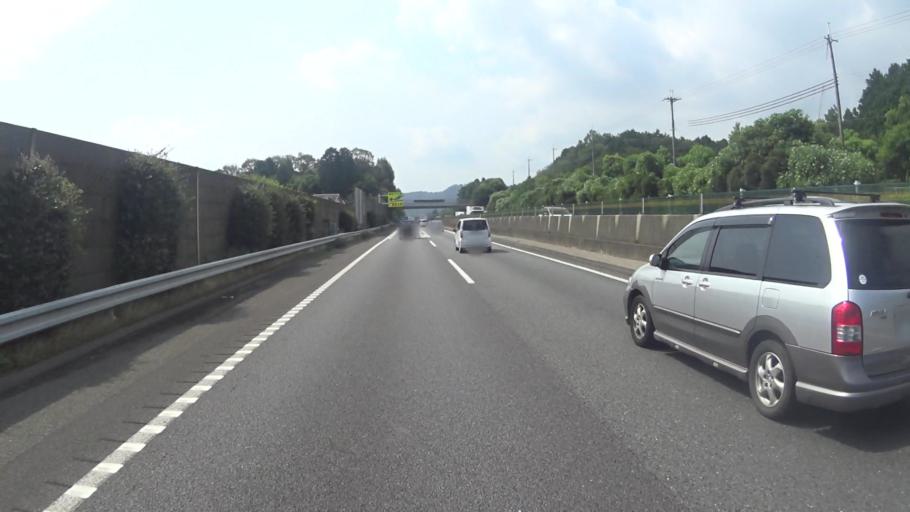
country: JP
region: Shiga Prefecture
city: Otsu-shi
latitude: 34.9847
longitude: 135.8801
